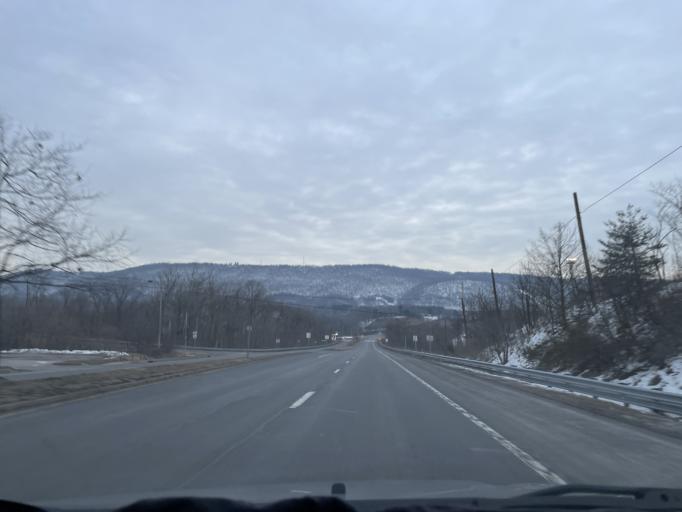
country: US
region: Maryland
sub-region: Allegany County
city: Cumberland
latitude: 39.6288
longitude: -78.7429
